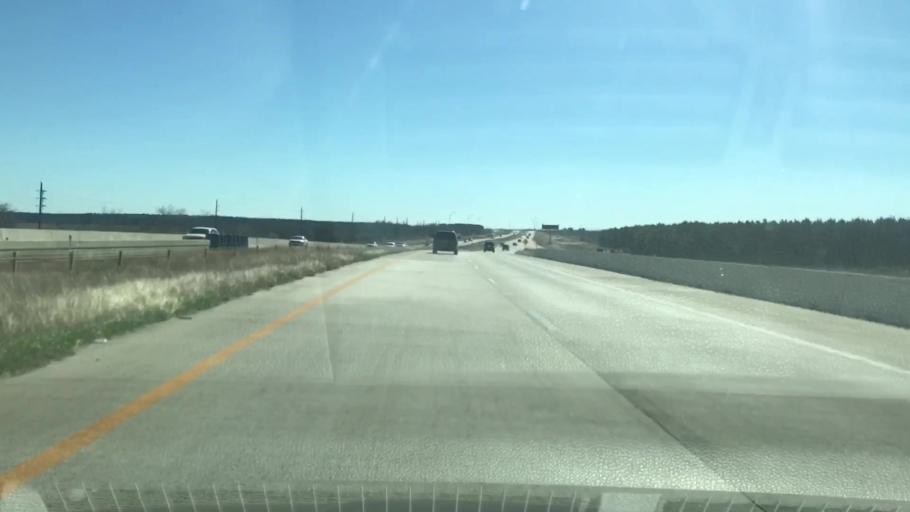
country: US
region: Texas
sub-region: Harris County
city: Cypress
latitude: 29.9036
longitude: -95.7585
